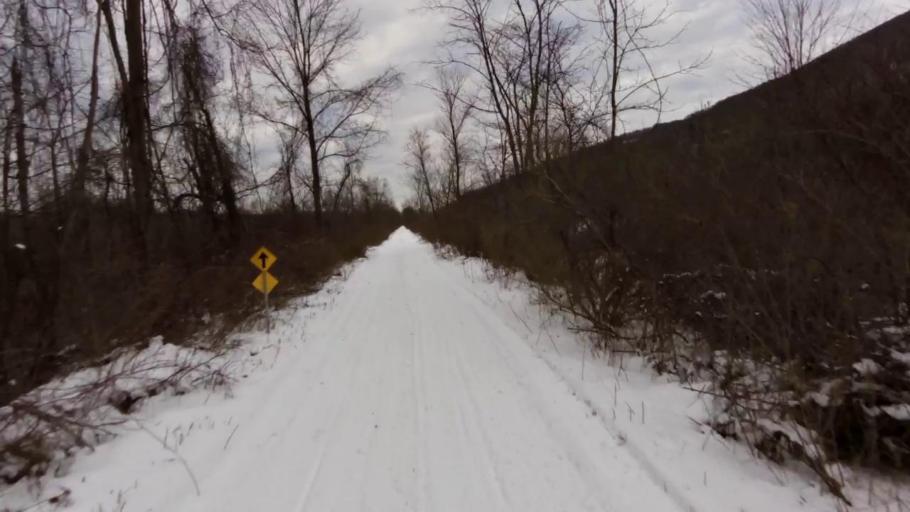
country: US
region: Pennsylvania
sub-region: McKean County
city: Foster Brook
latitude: 42.0027
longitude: -78.6223
